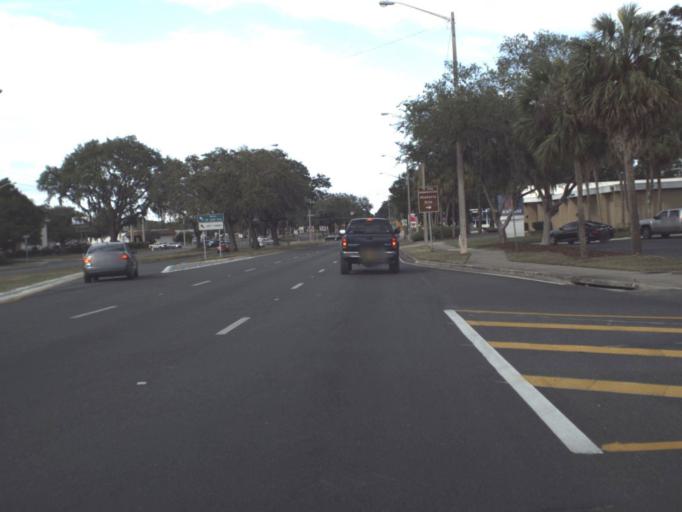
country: US
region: Florida
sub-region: Marion County
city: Ocala
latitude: 29.1959
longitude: -82.0887
